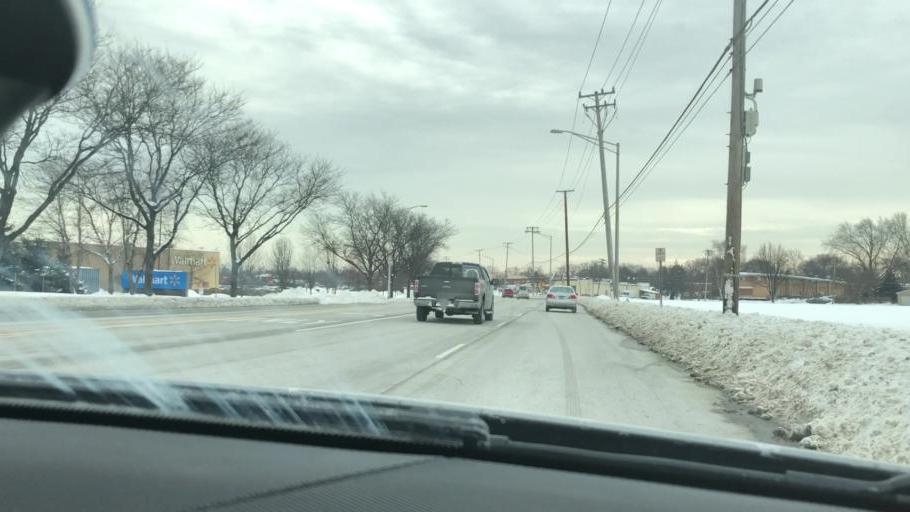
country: US
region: Illinois
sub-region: Cook County
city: Mount Prospect
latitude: 42.0696
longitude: -87.9255
